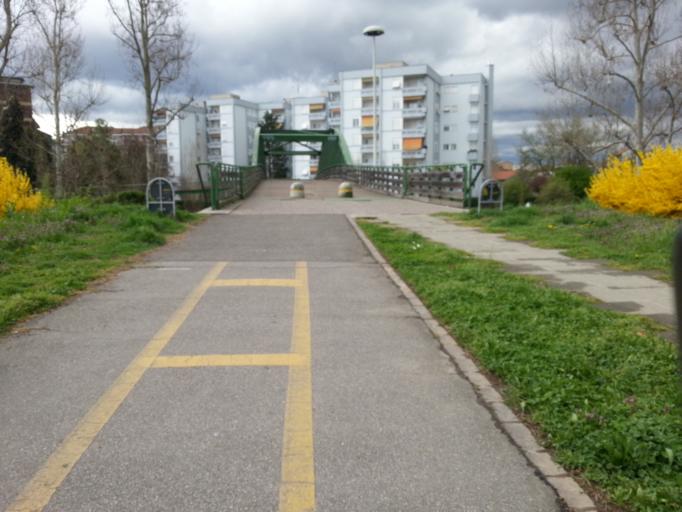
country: IT
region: Lombardy
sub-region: Citta metropolitana di Milano
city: Bresso
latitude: 45.5158
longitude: 9.1795
